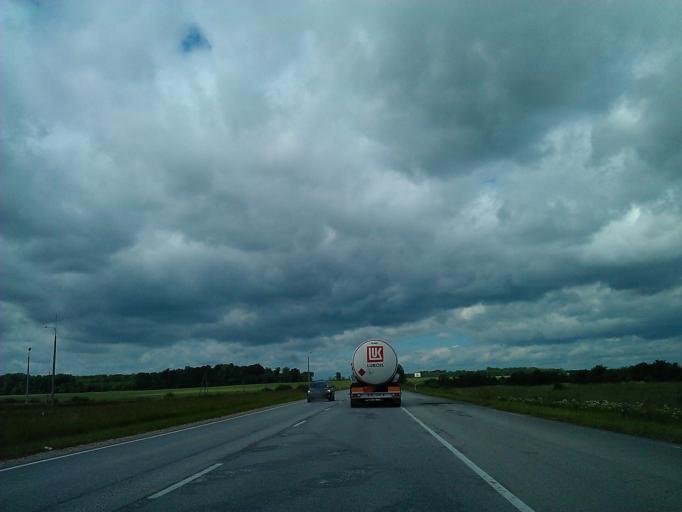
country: LV
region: Engure
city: Smarde
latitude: 56.9166
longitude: 23.3240
